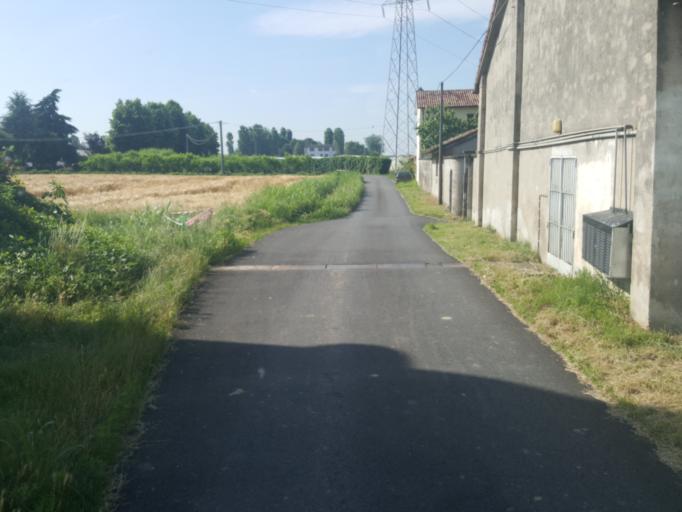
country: IT
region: Lombardy
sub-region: Provincia di Cremona
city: Crema
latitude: 45.3476
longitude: 9.6705
